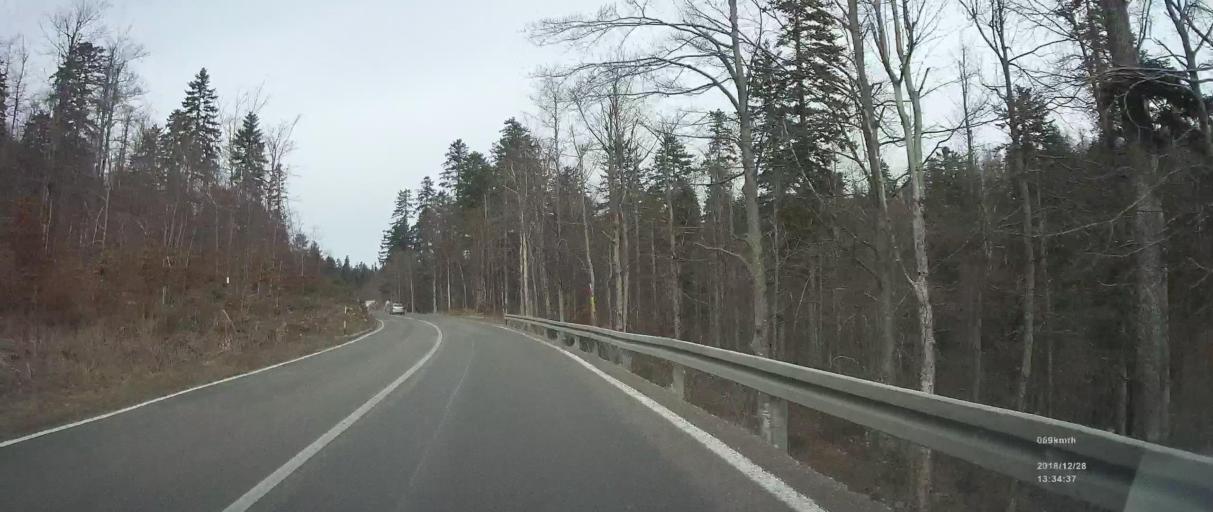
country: HR
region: Primorsko-Goranska
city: Hreljin
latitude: 45.3422
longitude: 14.6912
